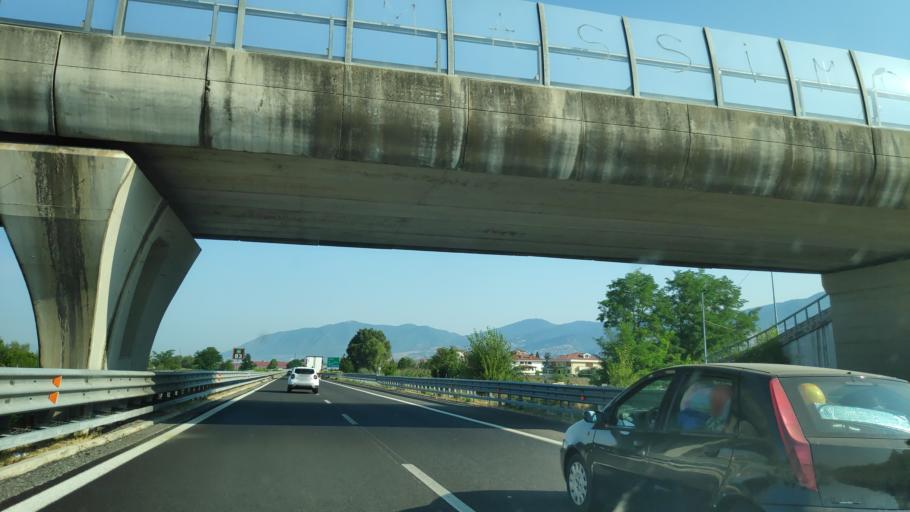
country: IT
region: Campania
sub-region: Provincia di Salerno
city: Buonabitacolo
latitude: 40.2873
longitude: 15.6503
